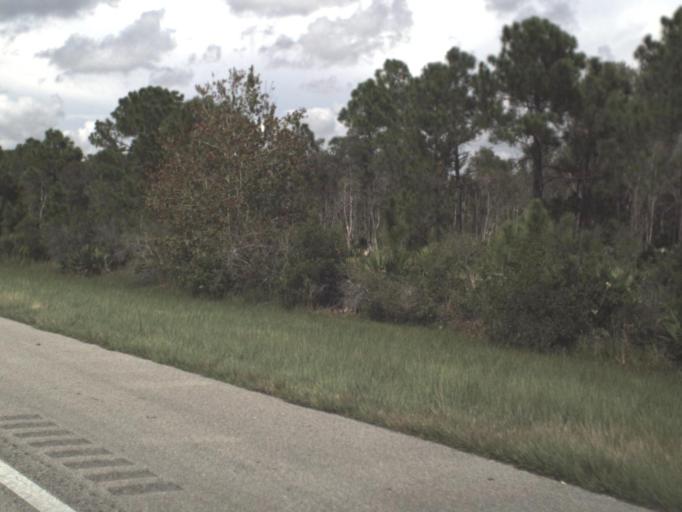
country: US
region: Florida
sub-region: Lee County
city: Suncoast Estates
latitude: 26.7729
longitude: -81.8828
